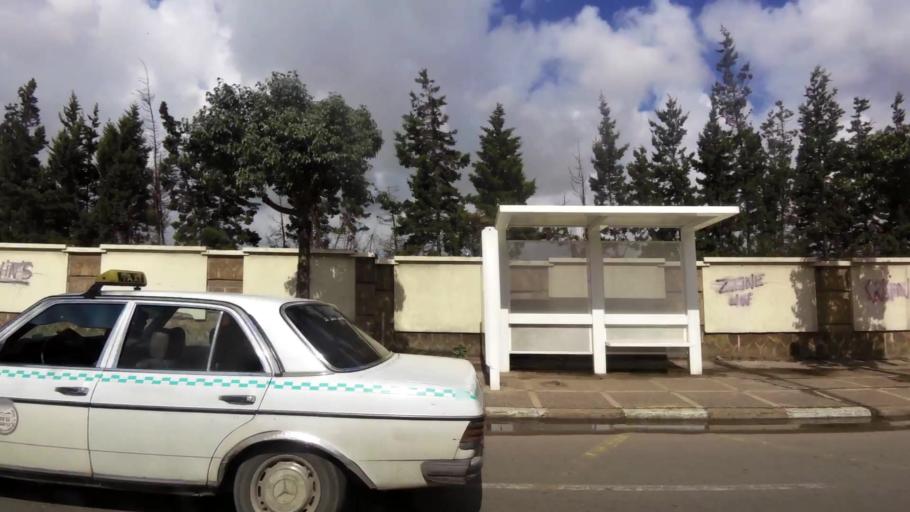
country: MA
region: Grand Casablanca
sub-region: Nouaceur
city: Bouskoura
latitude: 33.5194
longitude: -7.6527
